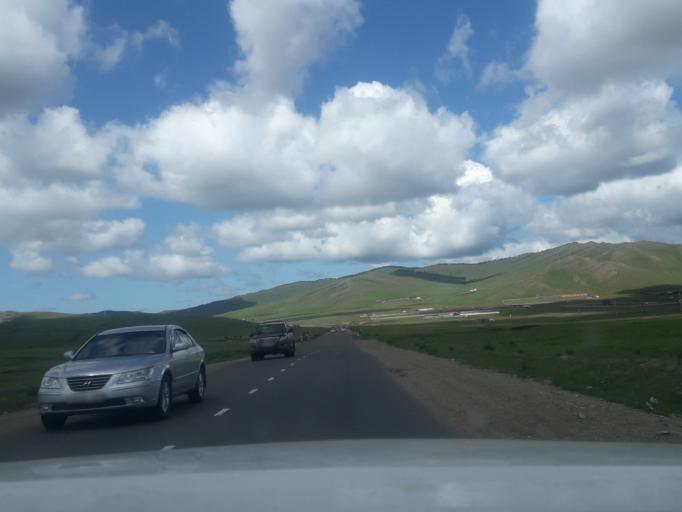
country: MN
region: Central Aimak
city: Ihsueuej
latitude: 48.1623
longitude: 106.4042
